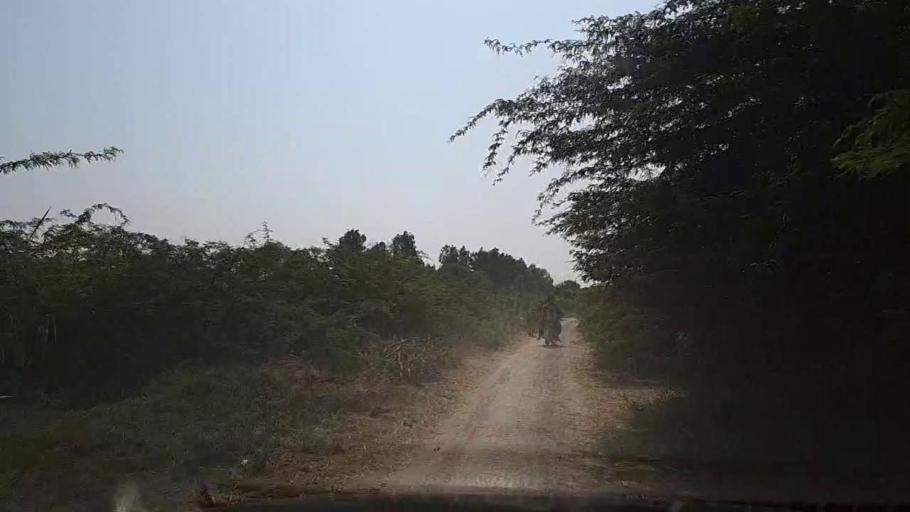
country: PK
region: Sindh
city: Thatta
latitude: 24.7785
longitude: 67.8276
